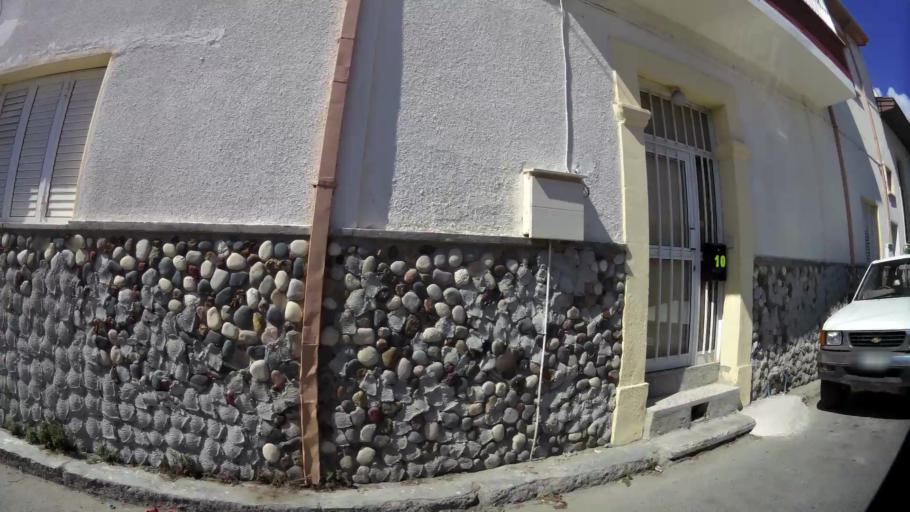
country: CY
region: Larnaka
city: Larnaca
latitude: 34.9096
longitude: 33.6373
